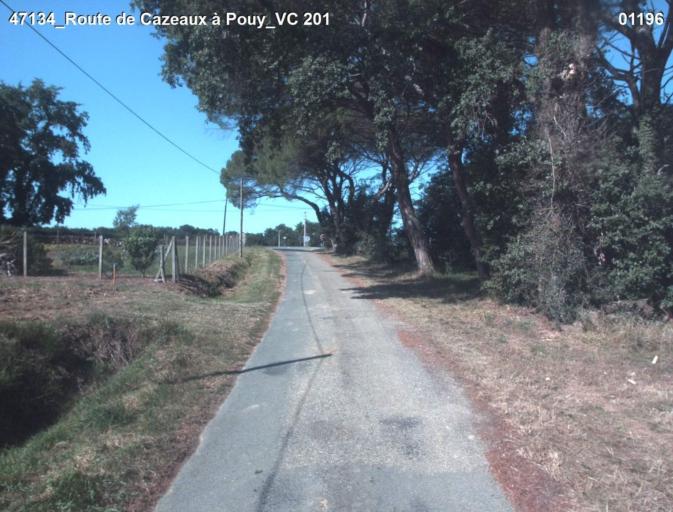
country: FR
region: Aquitaine
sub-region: Departement du Lot-et-Garonne
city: Mezin
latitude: 44.0156
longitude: 0.3050
